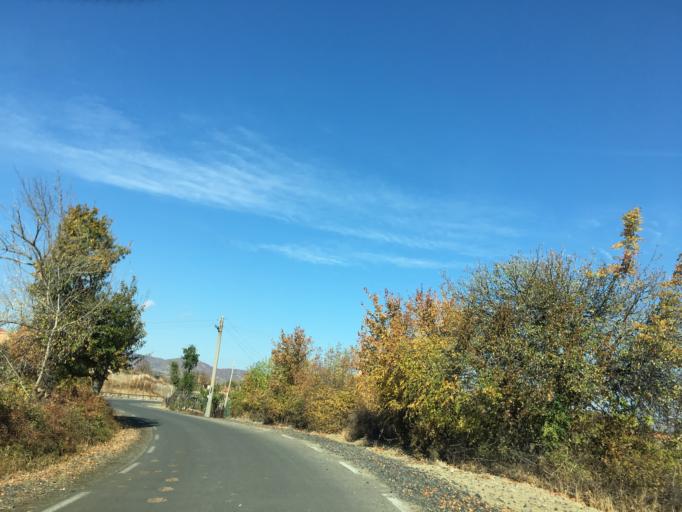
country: BG
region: Kurdzhali
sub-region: Obshtina Krumovgrad
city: Krumovgrad
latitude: 41.4985
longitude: 25.5247
